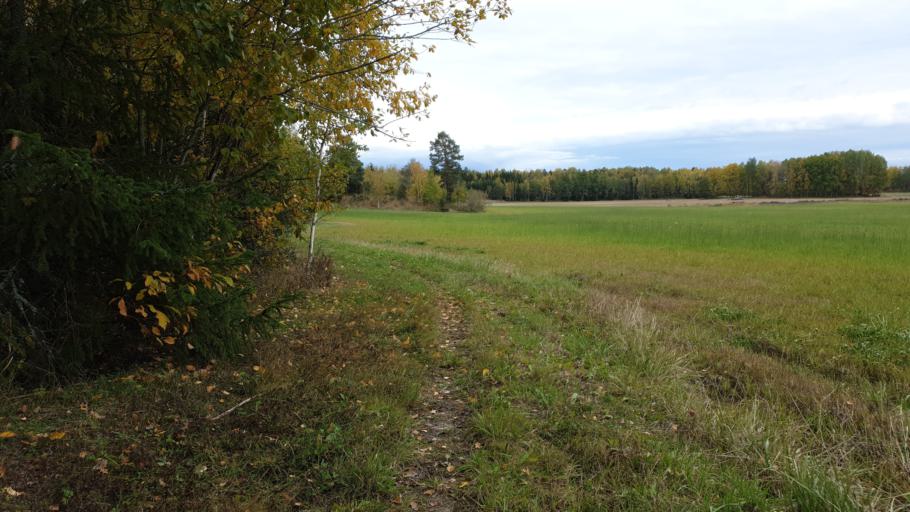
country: SE
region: Vaestmanland
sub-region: Sala Kommun
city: Sala
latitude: 59.8160
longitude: 16.6495
